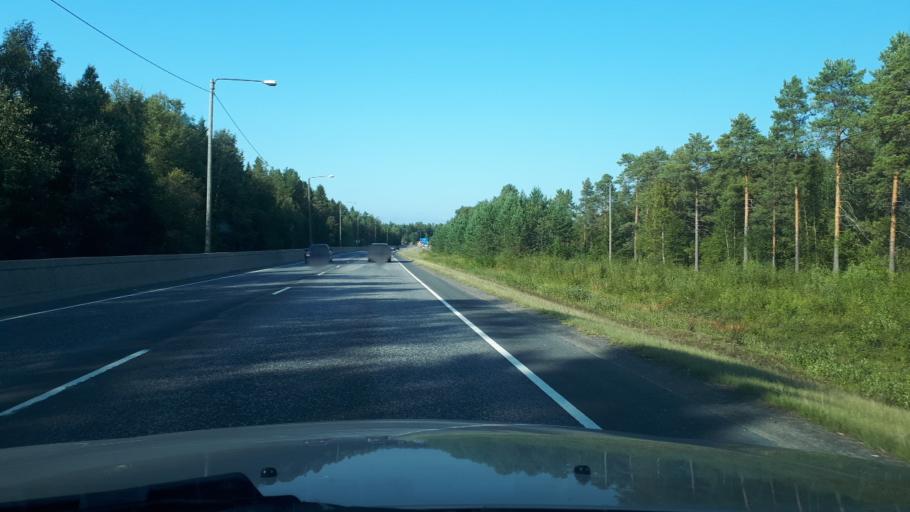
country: FI
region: Northern Ostrobothnia
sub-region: Oulunkaari
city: Ii
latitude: 65.3131
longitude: 25.3735
